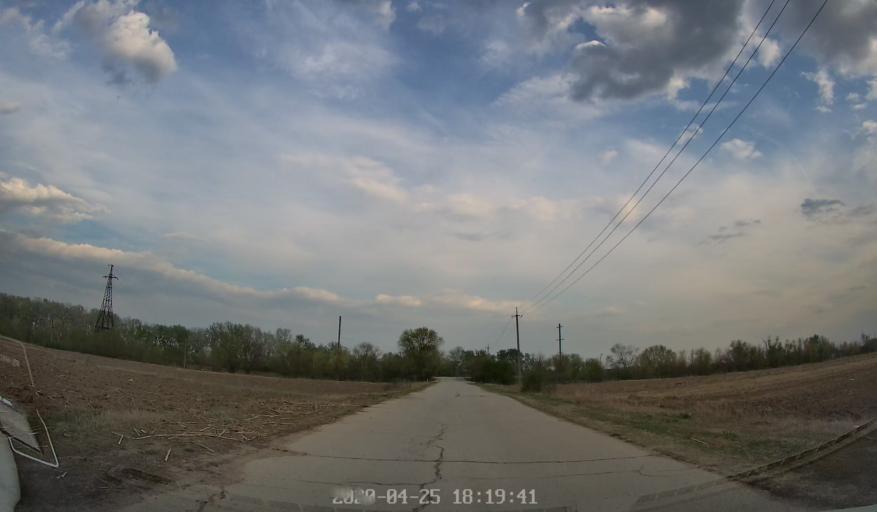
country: MD
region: Criuleni
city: Criuleni
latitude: 47.1586
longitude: 29.1318
